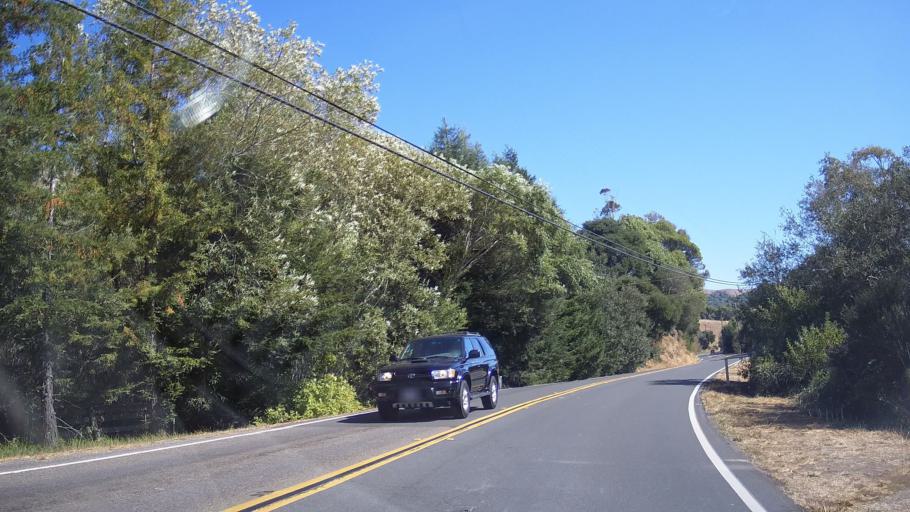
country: US
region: California
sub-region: Marin County
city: Inverness
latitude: 38.0827
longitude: -122.7813
